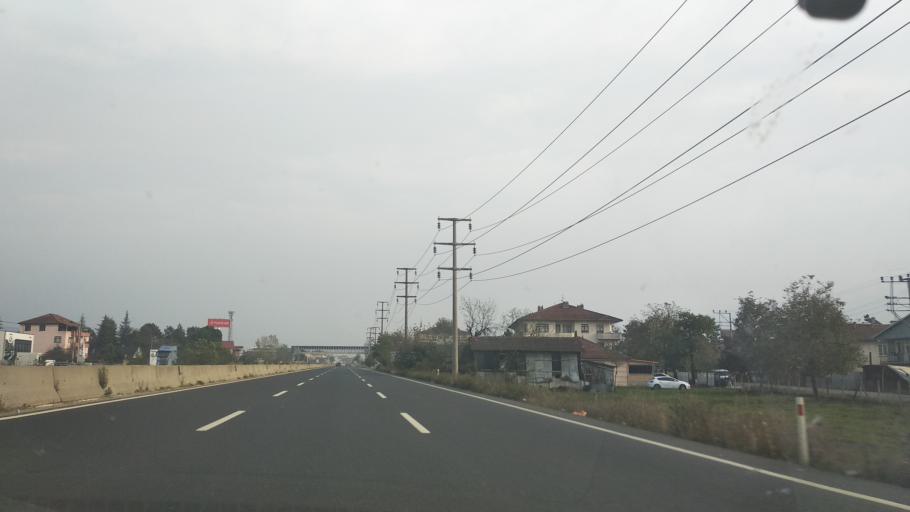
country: TR
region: Duzce
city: Duzce
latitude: 40.8073
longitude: 31.2296
